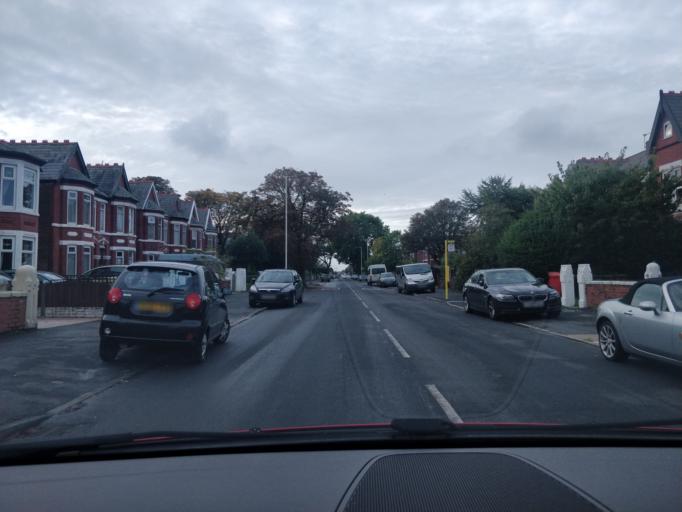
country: GB
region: England
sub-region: Sefton
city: Southport
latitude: 53.6405
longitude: -2.9823
